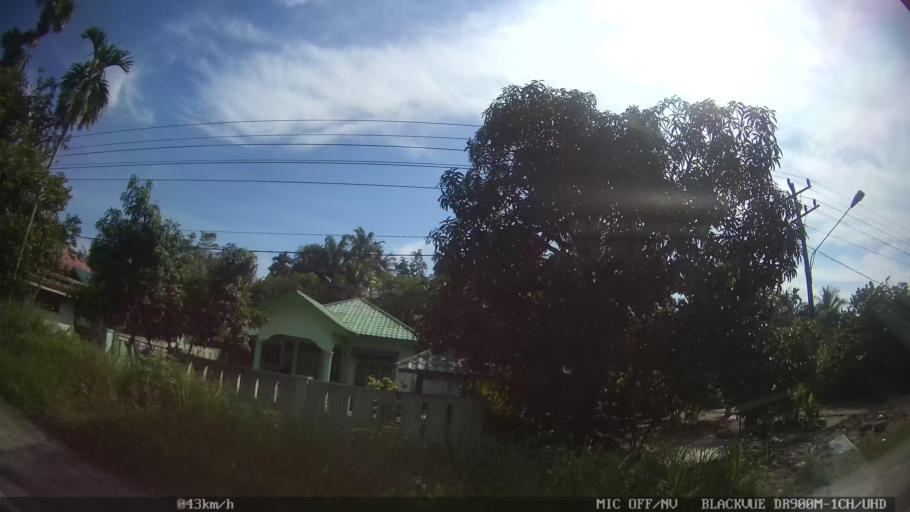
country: ID
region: North Sumatra
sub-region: Kabupaten Langkat
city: Stabat
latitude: 3.7250
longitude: 98.4993
